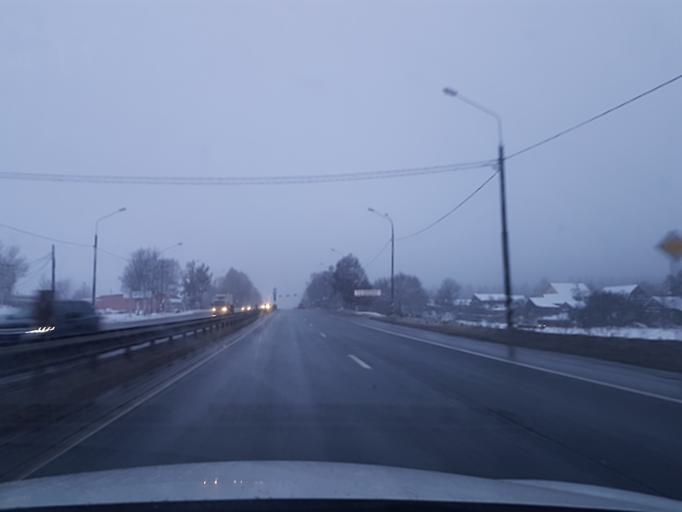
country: RU
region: Moskovskaya
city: Solnechnogorsk
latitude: 56.2328
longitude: 36.9048
